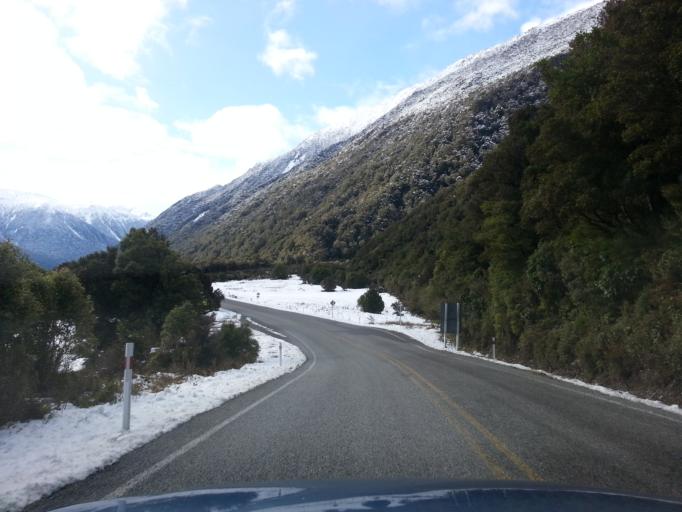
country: NZ
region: West Coast
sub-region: Grey District
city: Greymouth
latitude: -42.8549
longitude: 171.5598
